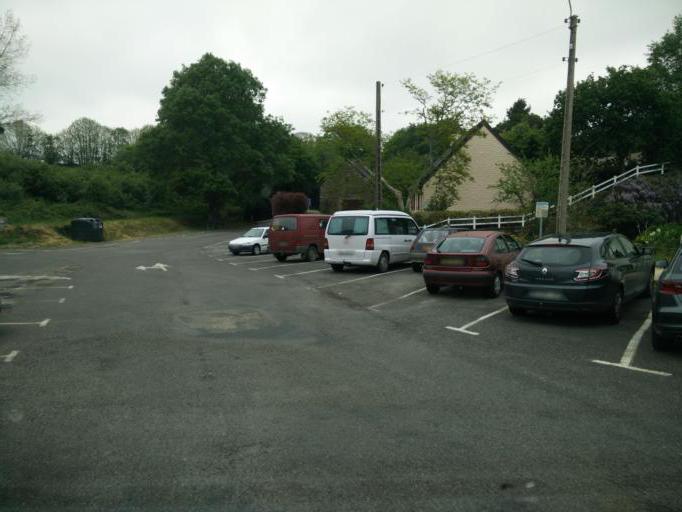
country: FR
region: Brittany
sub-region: Departement du Finistere
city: Pont-Aven
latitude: 47.8629
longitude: -3.7660
